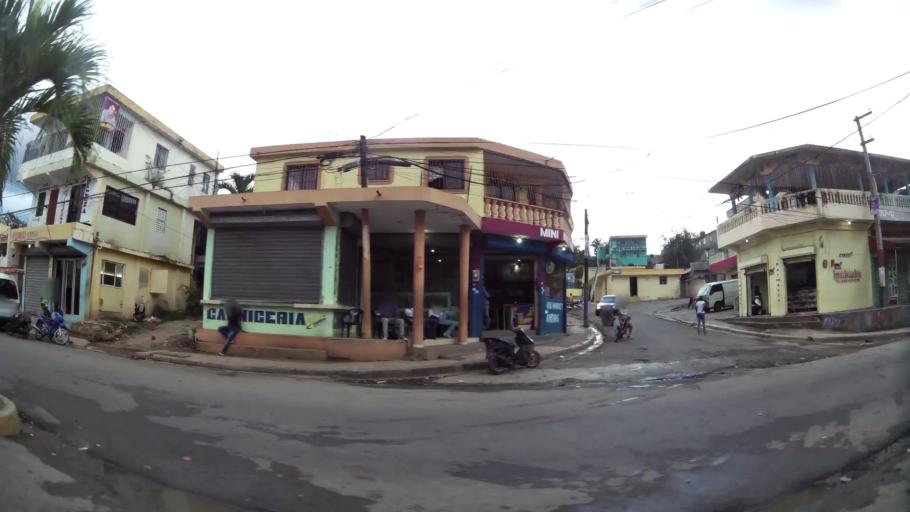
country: DO
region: San Cristobal
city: Villa Altagracia
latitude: 18.6615
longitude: -70.1698
